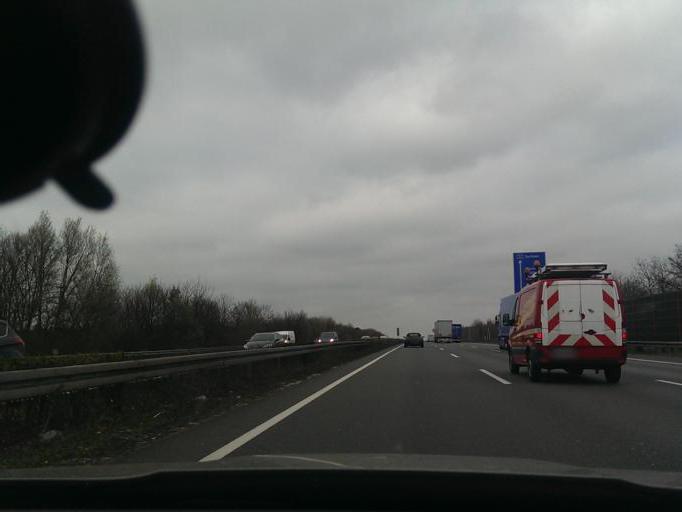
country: DE
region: Lower Saxony
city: Gross Munzel
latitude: 52.4053
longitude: 9.5029
